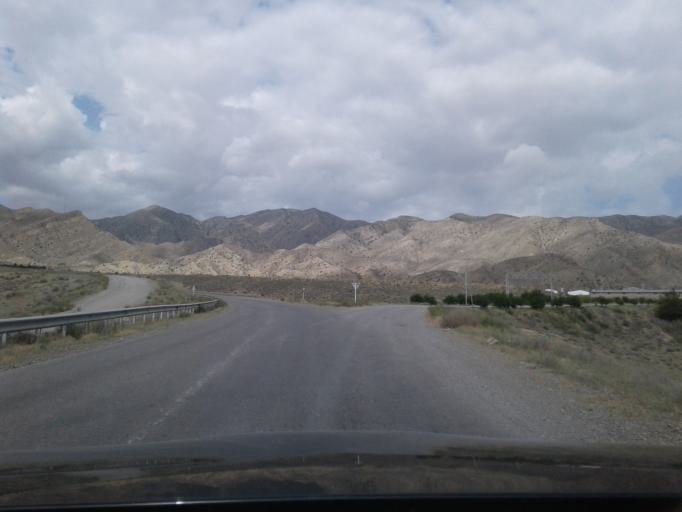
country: TM
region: Ahal
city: Baharly
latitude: 38.5092
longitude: 57.0778
